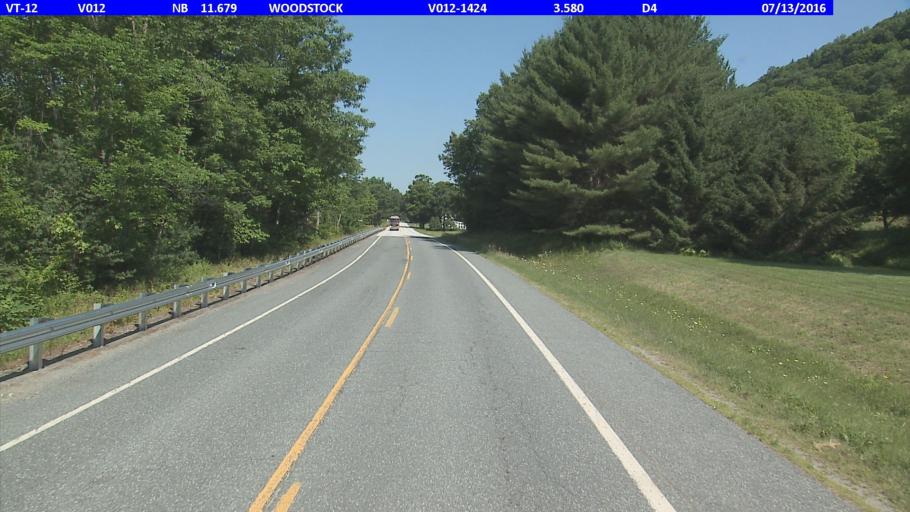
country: US
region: Vermont
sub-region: Windsor County
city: Woodstock
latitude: 43.6522
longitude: -72.5632
